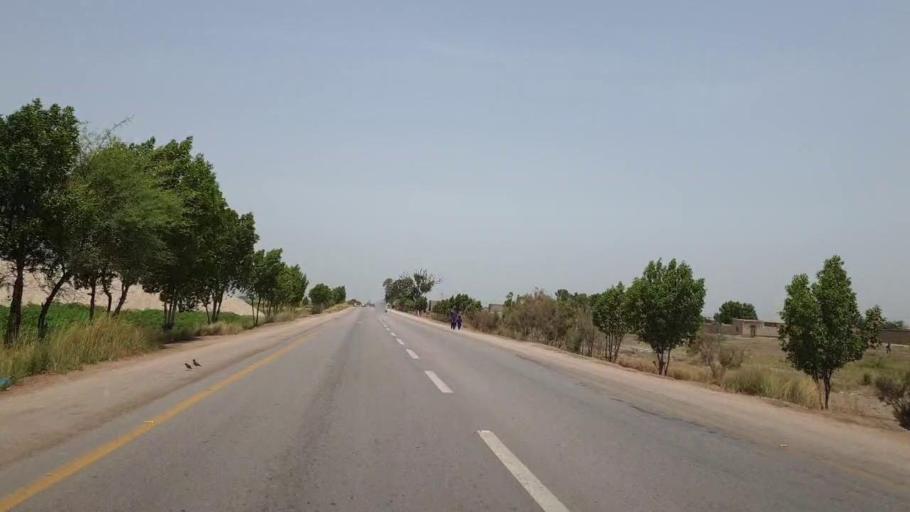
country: PK
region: Sindh
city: Nawabshah
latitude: 26.2260
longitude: 68.4921
